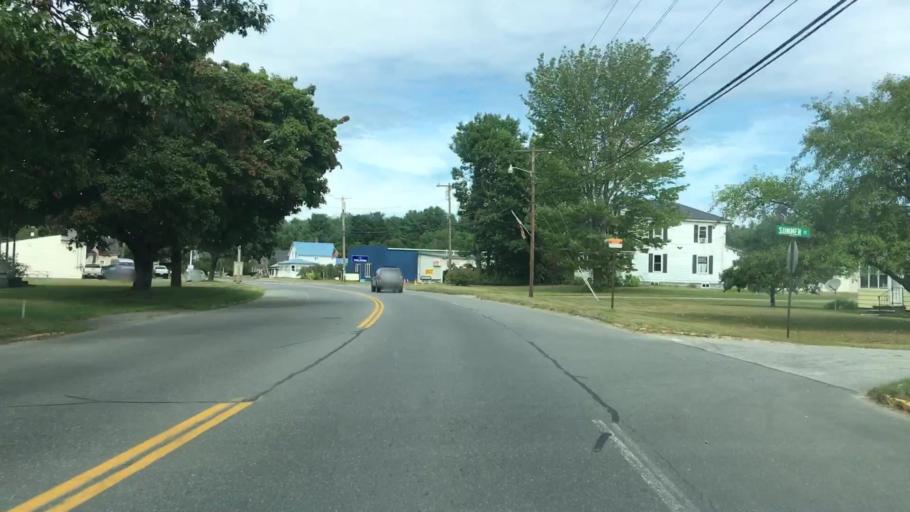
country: US
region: Maine
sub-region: Piscataquis County
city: Milo
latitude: 45.2602
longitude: -68.9880
